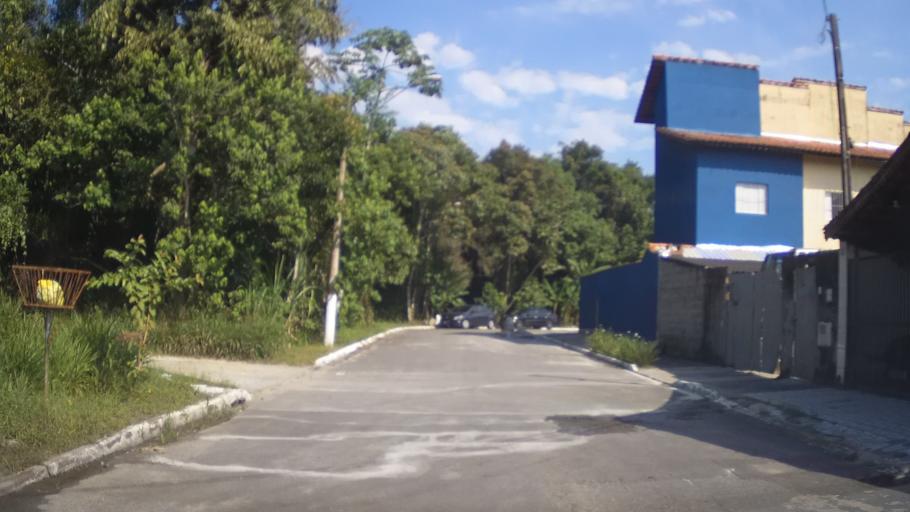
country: BR
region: Sao Paulo
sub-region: Praia Grande
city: Praia Grande
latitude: -23.9923
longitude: -46.4135
